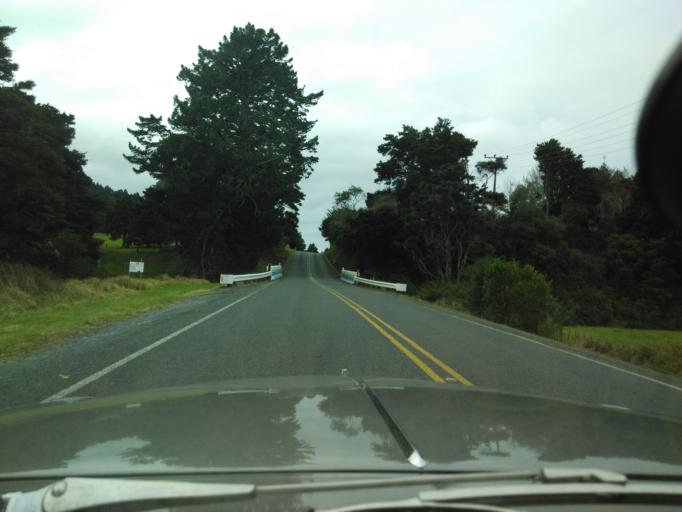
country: NZ
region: Auckland
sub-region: Auckland
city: Parakai
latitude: -36.6326
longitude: 174.5528
